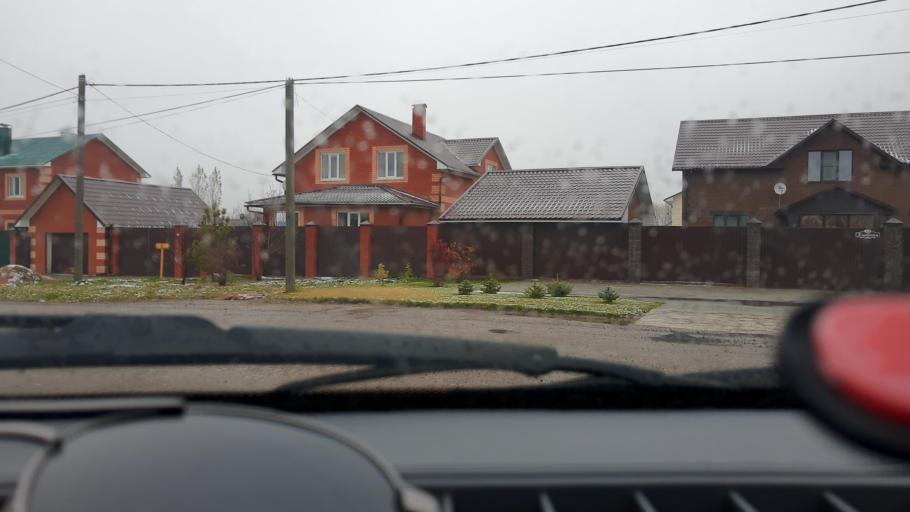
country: RU
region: Bashkortostan
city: Kabakovo
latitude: 54.6213
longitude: 56.1315
